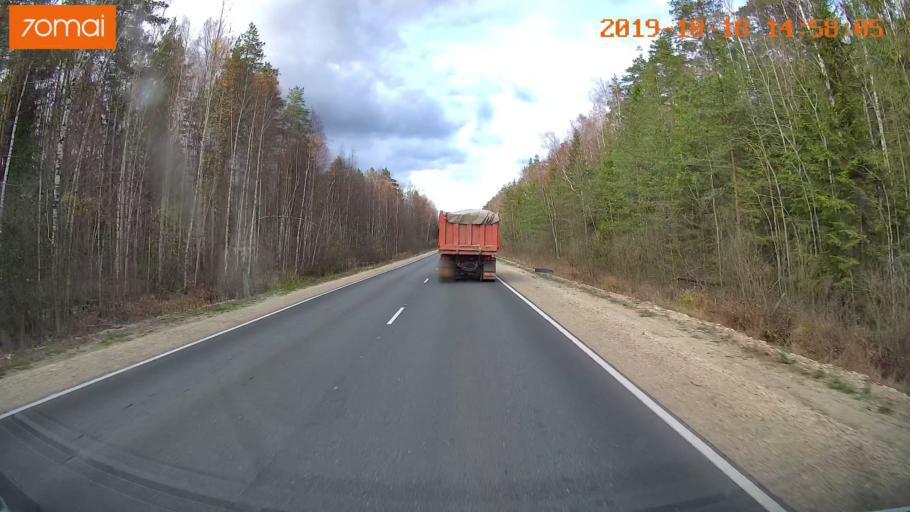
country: RU
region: Vladimir
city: Kurlovo
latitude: 55.4869
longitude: 40.5785
